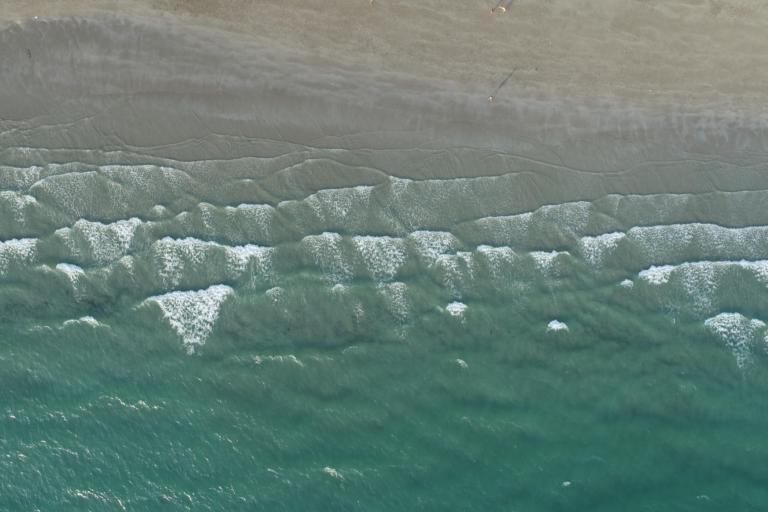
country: TH
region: Rayong
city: Rayong
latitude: 12.5986
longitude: 101.4053
